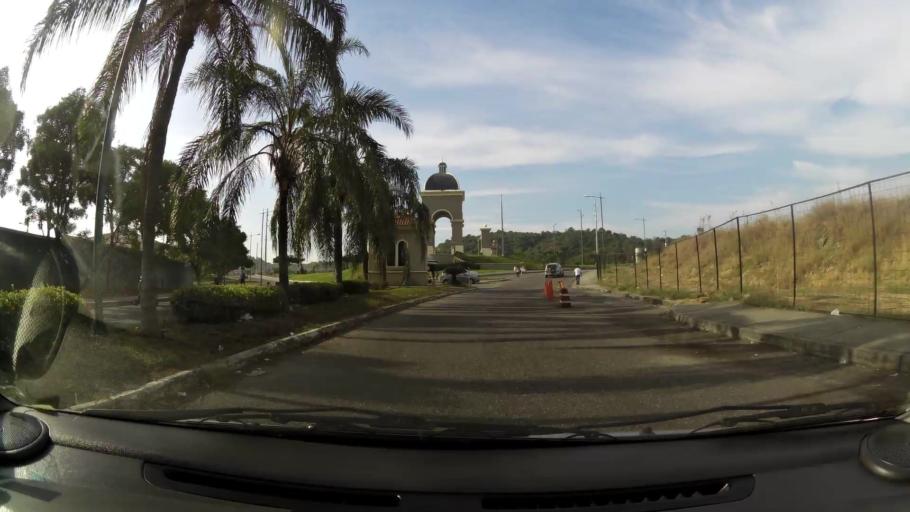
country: EC
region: Guayas
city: Eloy Alfaro
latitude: -2.0666
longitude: -79.9126
